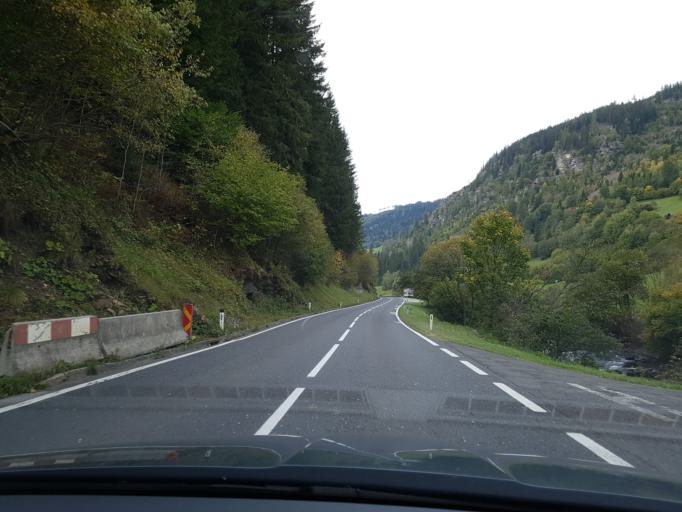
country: AT
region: Salzburg
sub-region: Politischer Bezirk Tamsweg
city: Ramingstein
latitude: 47.0716
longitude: 13.8655
